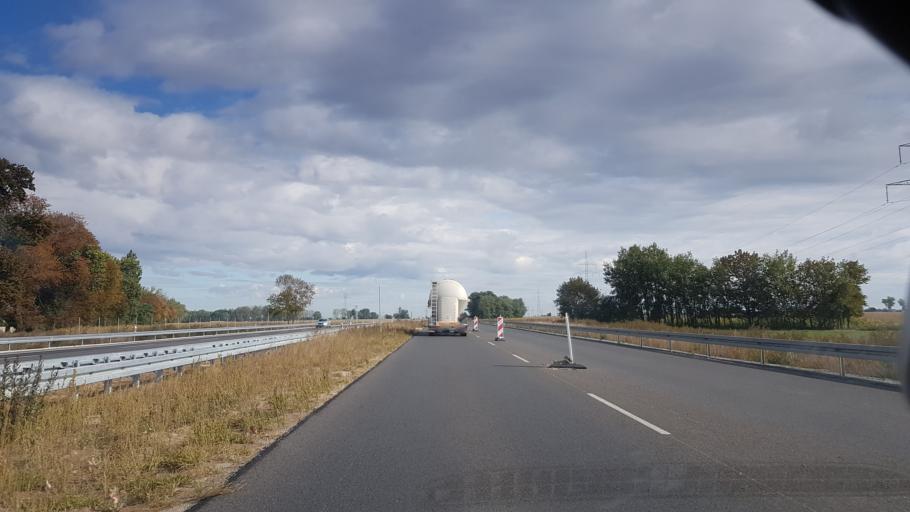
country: PL
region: Greater Poland Voivodeship
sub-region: Powiat poznanski
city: Steszew
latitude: 52.3177
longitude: 16.7121
